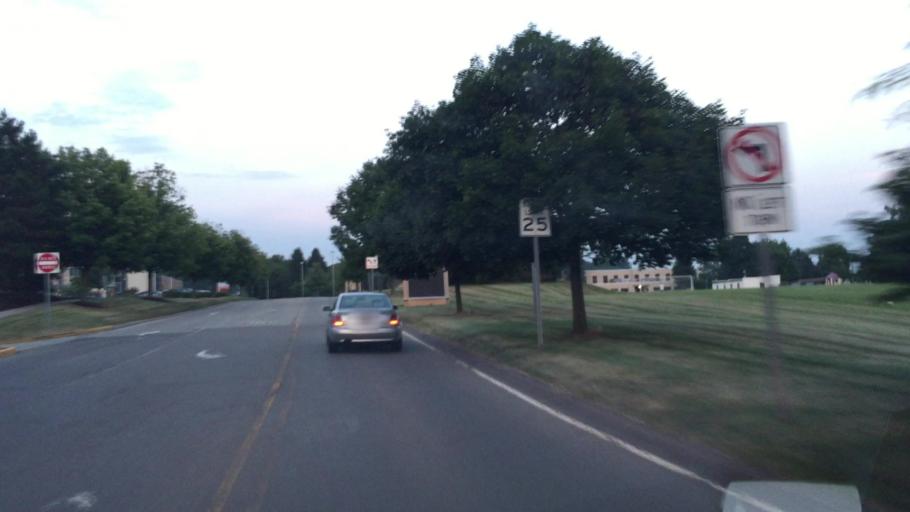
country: US
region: Pennsylvania
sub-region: Allegheny County
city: West View
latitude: 40.5720
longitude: -80.0159
